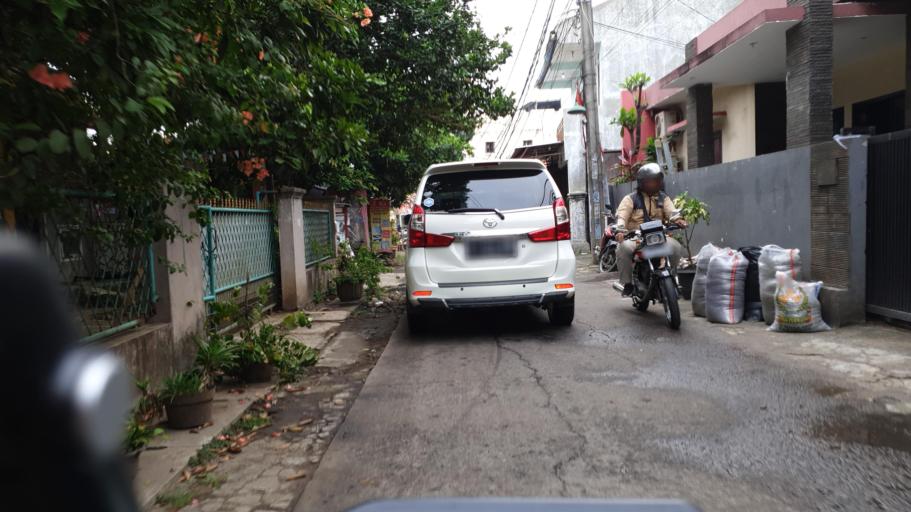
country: ID
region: West Java
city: Pamulang
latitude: -6.3305
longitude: 106.7692
